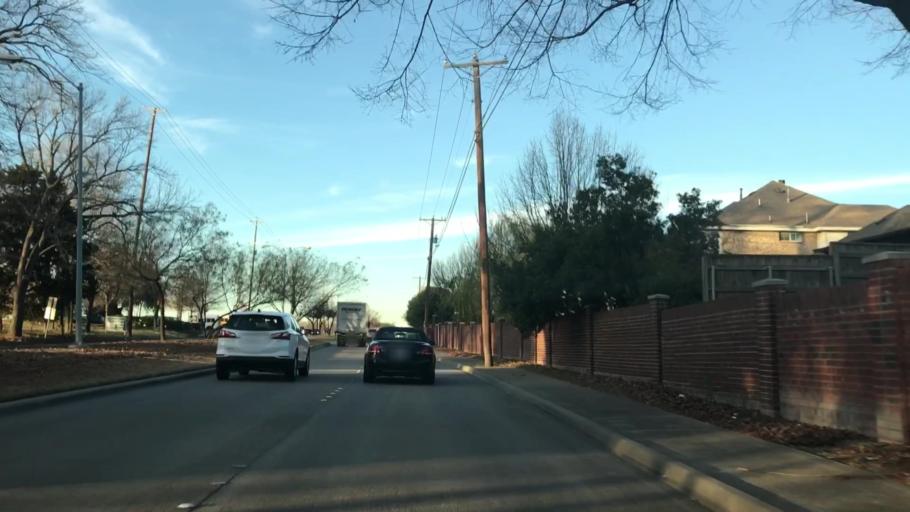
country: US
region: Texas
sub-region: Dallas County
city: Rowlett
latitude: 32.8967
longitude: -96.5181
